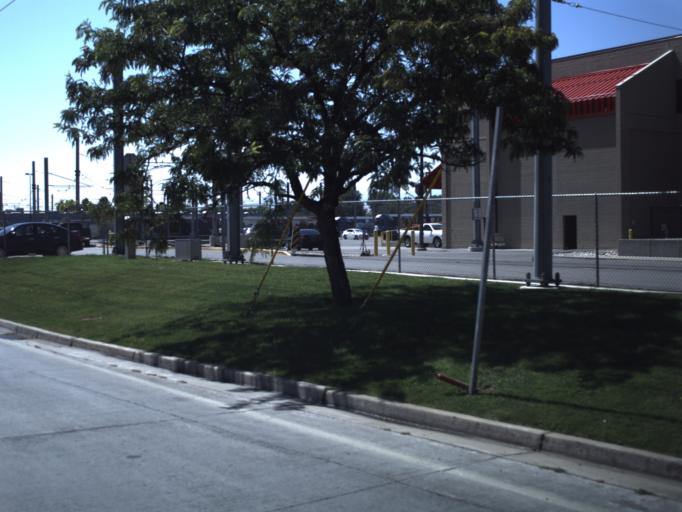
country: US
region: Utah
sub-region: Salt Lake County
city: South Salt Lake
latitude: 40.7225
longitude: -111.9175
